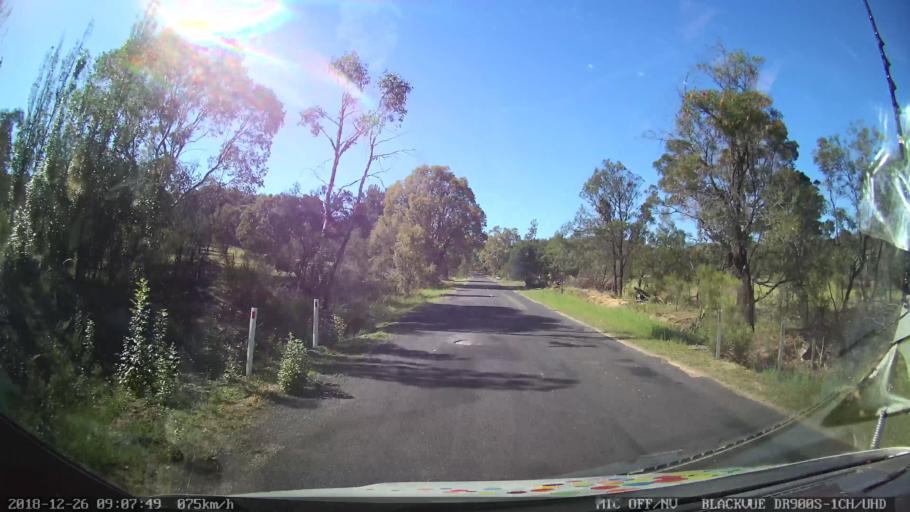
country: AU
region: New South Wales
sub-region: Mid-Western Regional
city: Kandos
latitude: -32.7097
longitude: 150.0030
